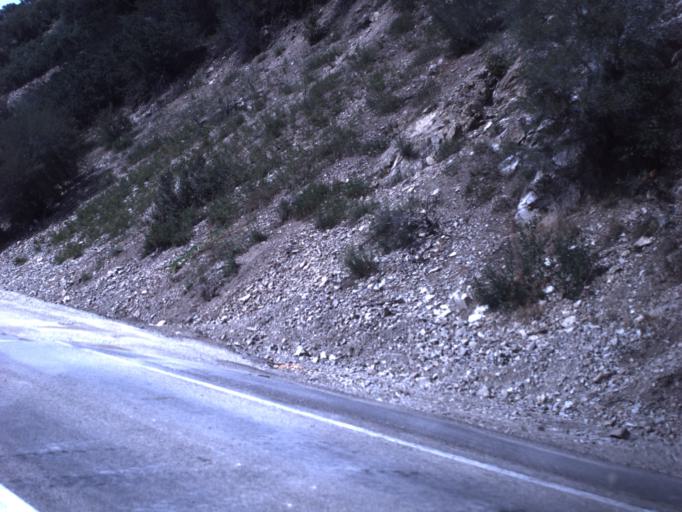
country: US
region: Utah
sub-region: Wasatch County
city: Heber
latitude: 40.3683
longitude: -111.2908
